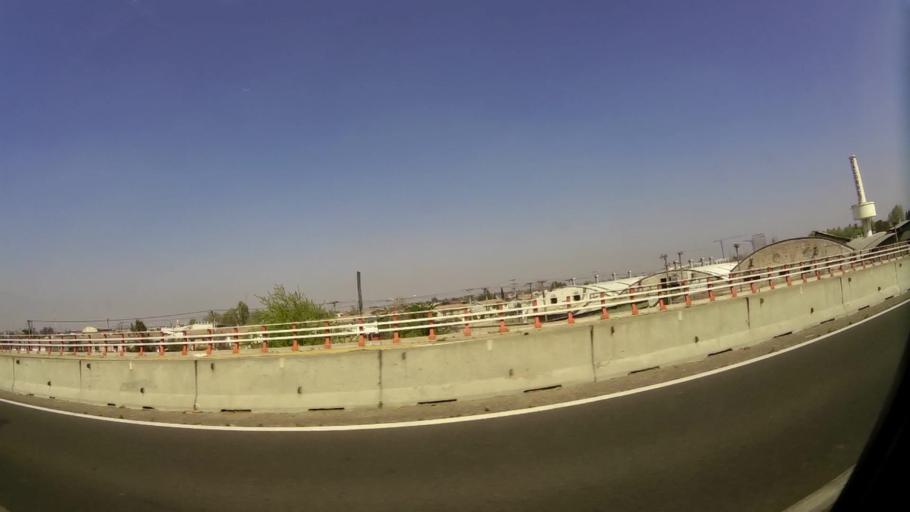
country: CL
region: Santiago Metropolitan
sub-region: Provincia de Santiago
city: Lo Prado
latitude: -33.4781
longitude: -70.6922
